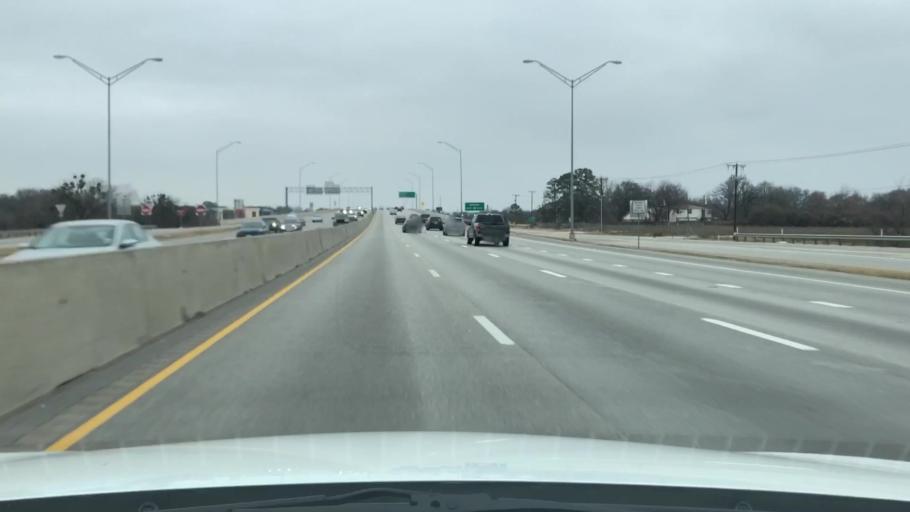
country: US
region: Texas
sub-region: Denton County
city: Corinth
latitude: 33.1479
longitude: -97.0570
